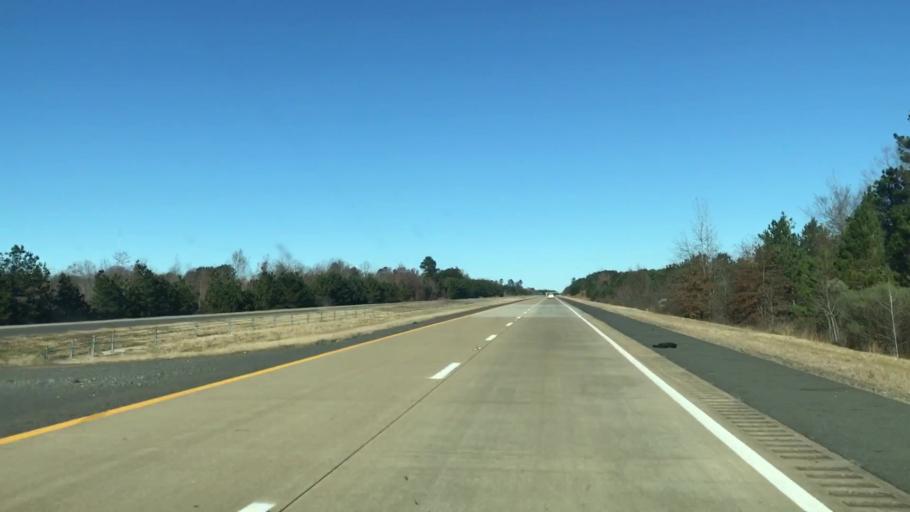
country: US
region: Texas
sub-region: Bowie County
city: Texarkana
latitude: 33.3013
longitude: -93.9302
